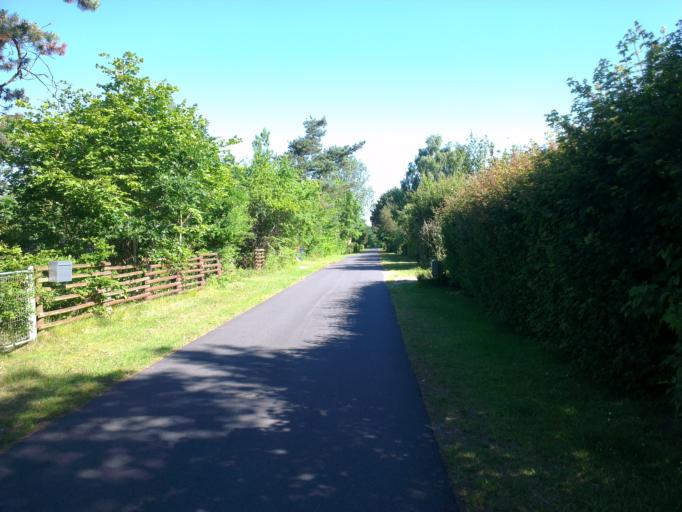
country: DK
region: Capital Region
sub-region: Halsnaes Kommune
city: Hundested
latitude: 55.9197
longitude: 11.9084
